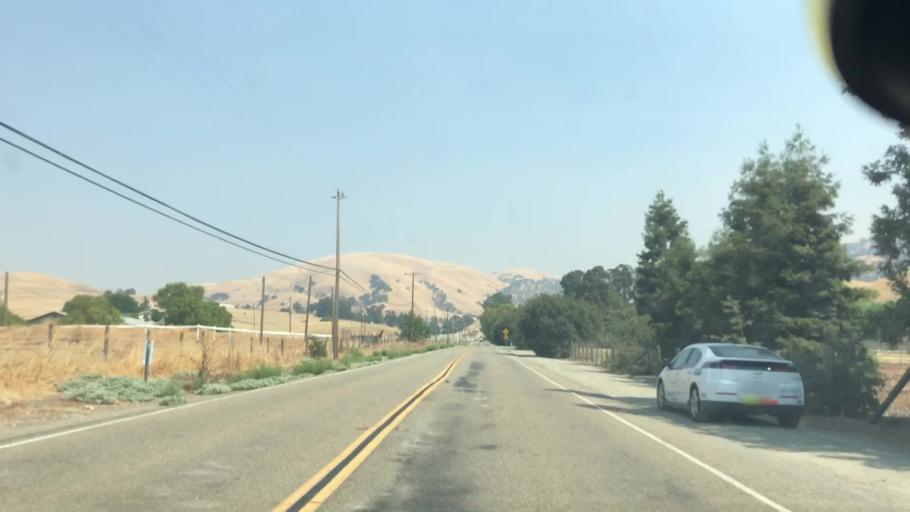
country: US
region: California
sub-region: Alameda County
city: Livermore
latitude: 37.6500
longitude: -121.6545
